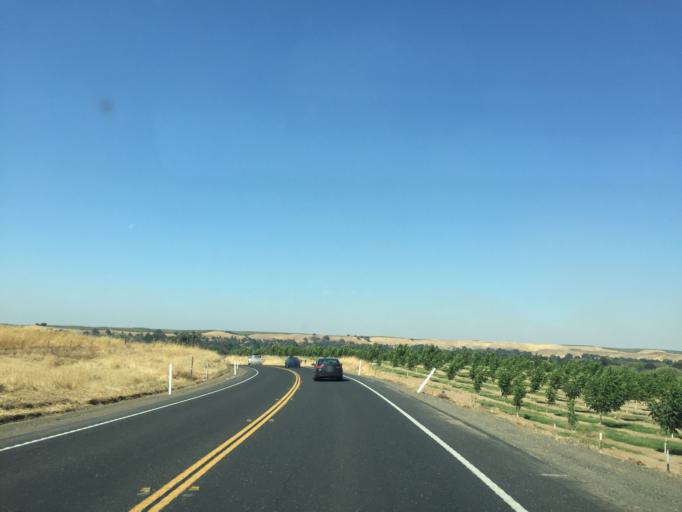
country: US
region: California
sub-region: Stanislaus County
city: East Oakdale
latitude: 37.8060
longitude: -120.7093
